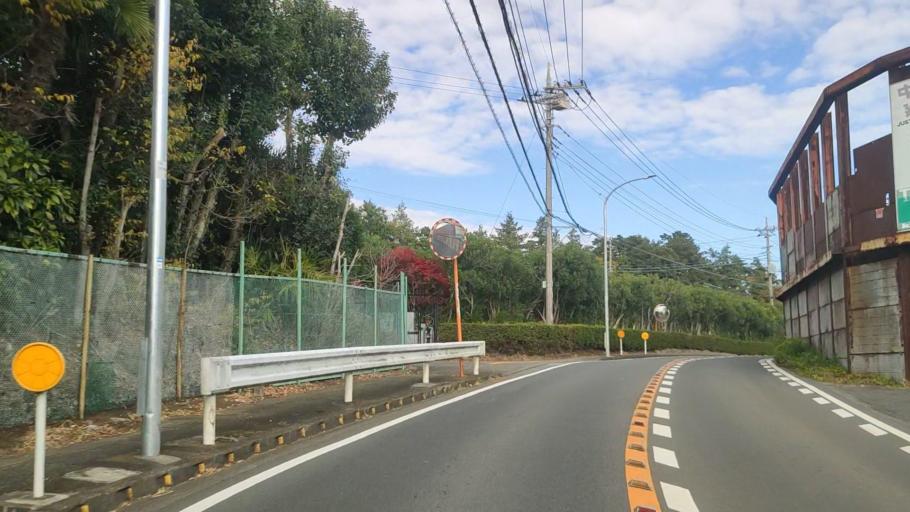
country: JP
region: Kanagawa
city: Minami-rinkan
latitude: 35.4884
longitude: 139.5039
